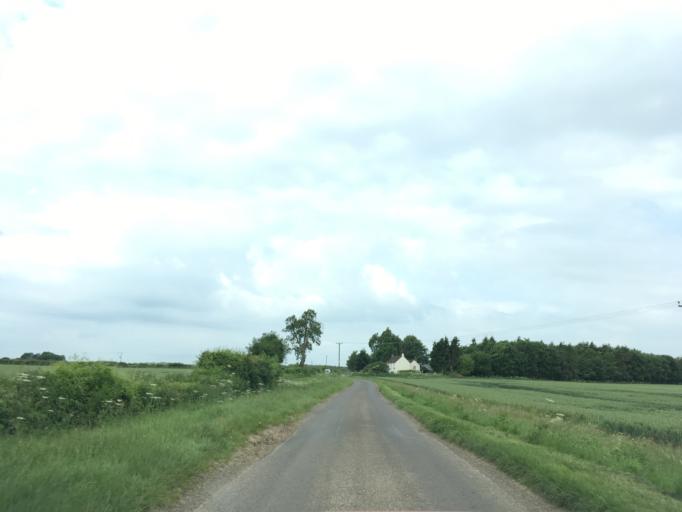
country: GB
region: England
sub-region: Gloucestershire
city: Nailsworth
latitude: 51.6602
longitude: -2.2059
